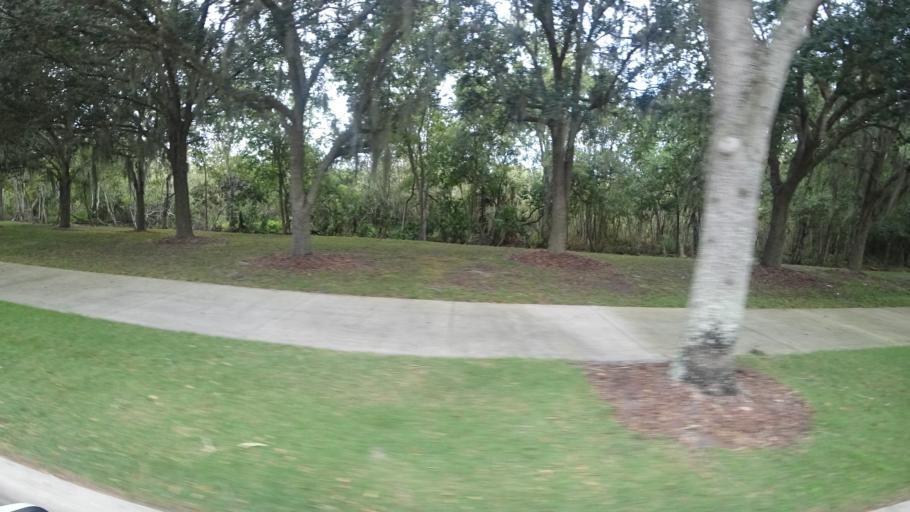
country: US
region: Florida
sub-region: Sarasota County
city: The Meadows
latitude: 27.3889
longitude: -82.4372
